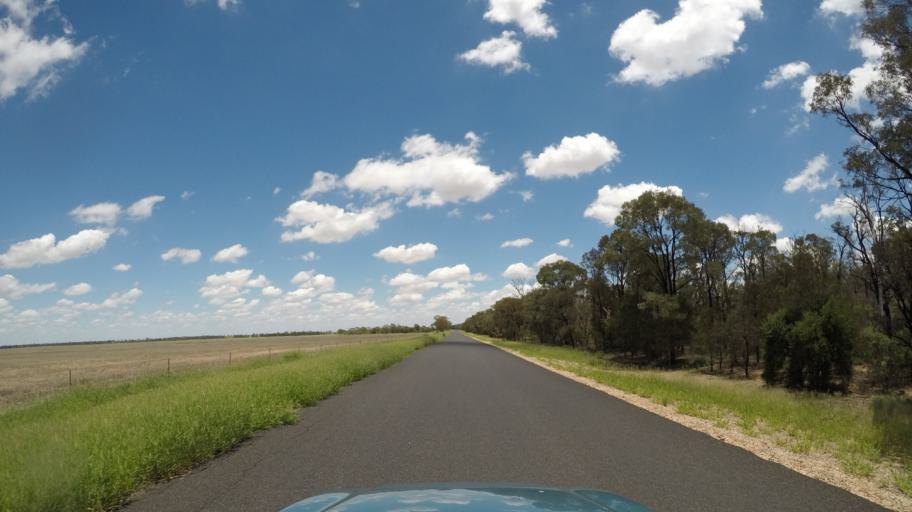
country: AU
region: Queensland
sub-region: Goondiwindi
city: Goondiwindi
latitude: -28.1575
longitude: 150.3855
